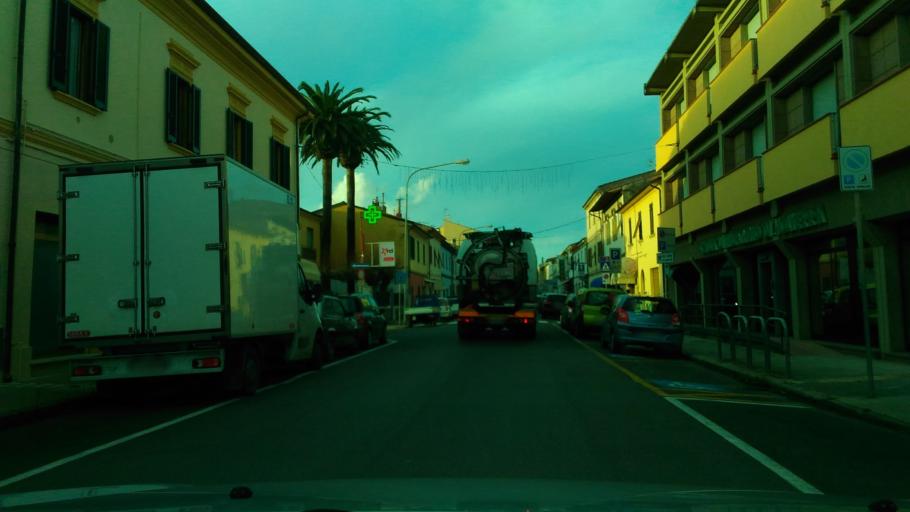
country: IT
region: Tuscany
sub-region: Provincia di Livorno
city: S.P. in Palazzi
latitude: 43.3250
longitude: 10.5088
